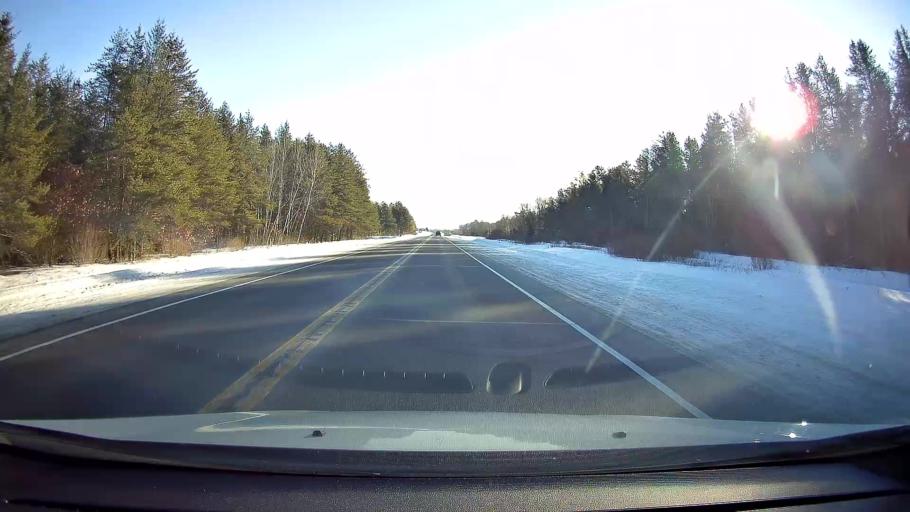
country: US
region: Wisconsin
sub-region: Sawyer County
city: Hayward
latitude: 45.9842
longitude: -91.5762
